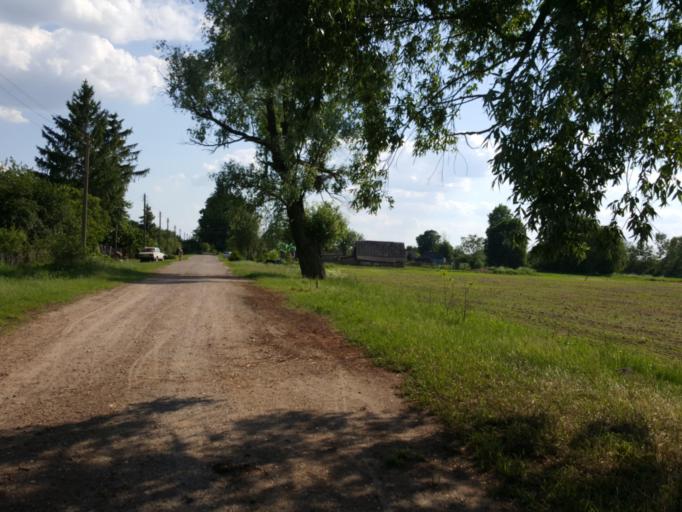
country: BY
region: Brest
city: Kamyanyets
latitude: 52.4503
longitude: 23.6144
